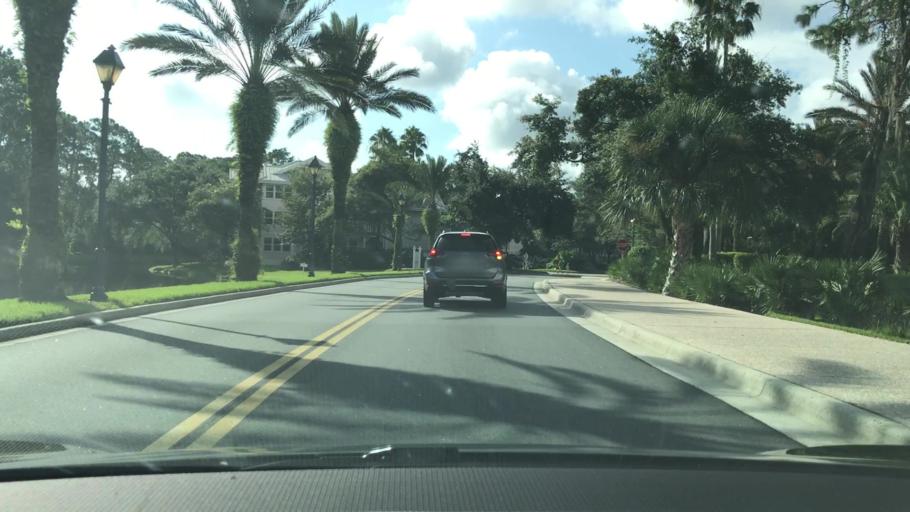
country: US
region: Florida
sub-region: Osceola County
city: Celebration
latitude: 28.3734
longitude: -81.5315
